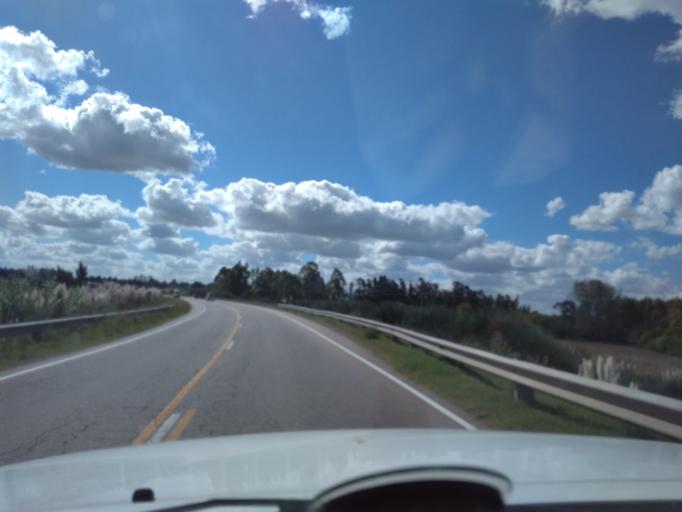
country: UY
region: Canelones
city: Sauce
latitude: -34.6735
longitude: -56.0517
